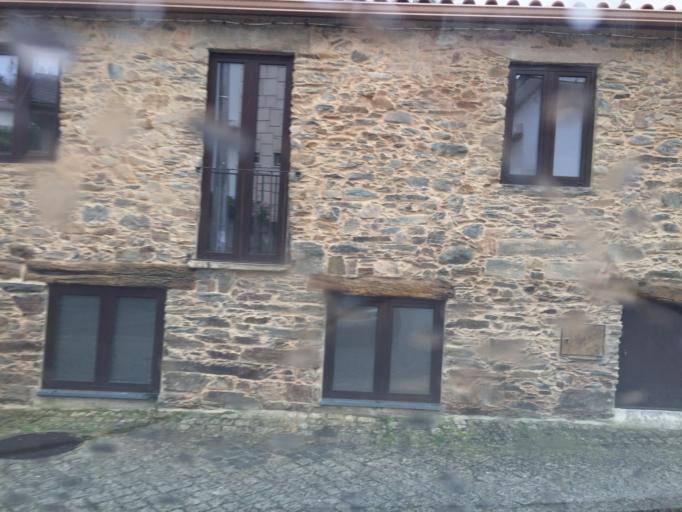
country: PT
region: Leiria
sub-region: Pedrogao Grande
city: Pedrogao Grande
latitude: 40.0167
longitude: -8.0991
